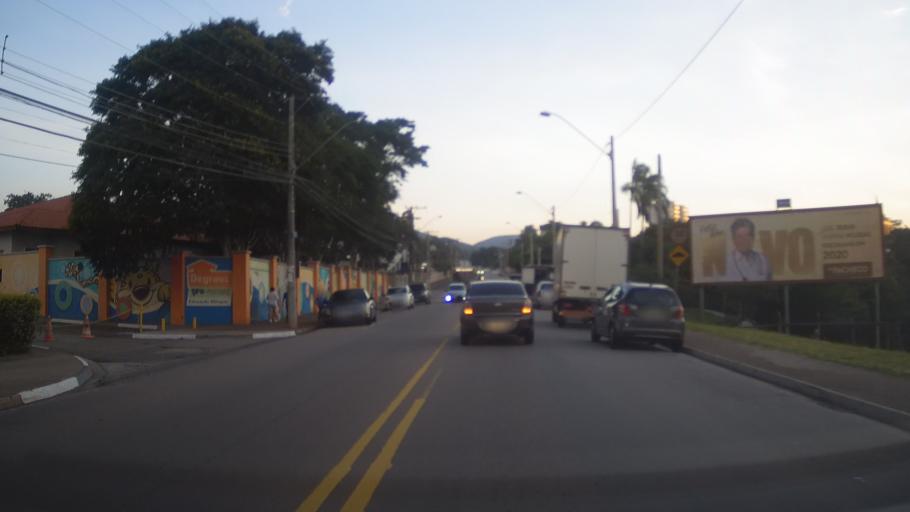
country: BR
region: Sao Paulo
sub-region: Jundiai
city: Jundiai
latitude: -23.1889
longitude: -46.9603
